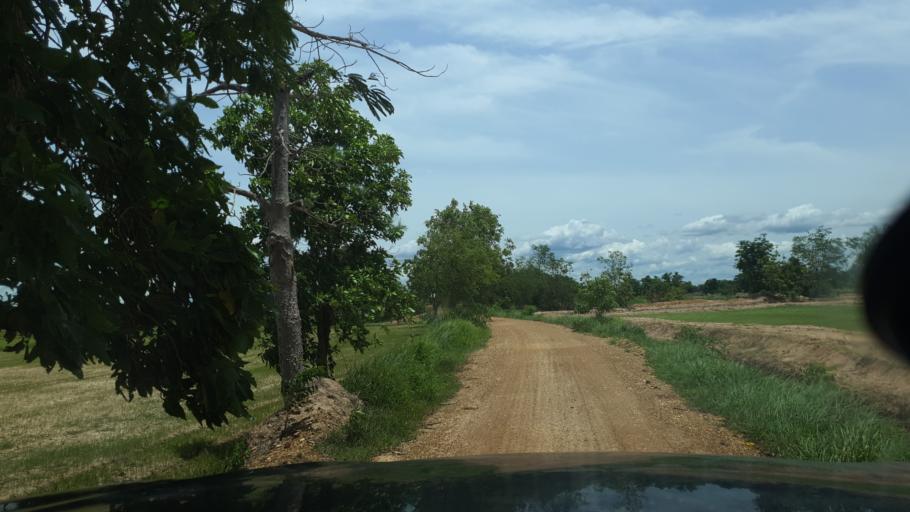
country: TH
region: Sukhothai
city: Ban Na
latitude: 17.1316
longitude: 99.6705
